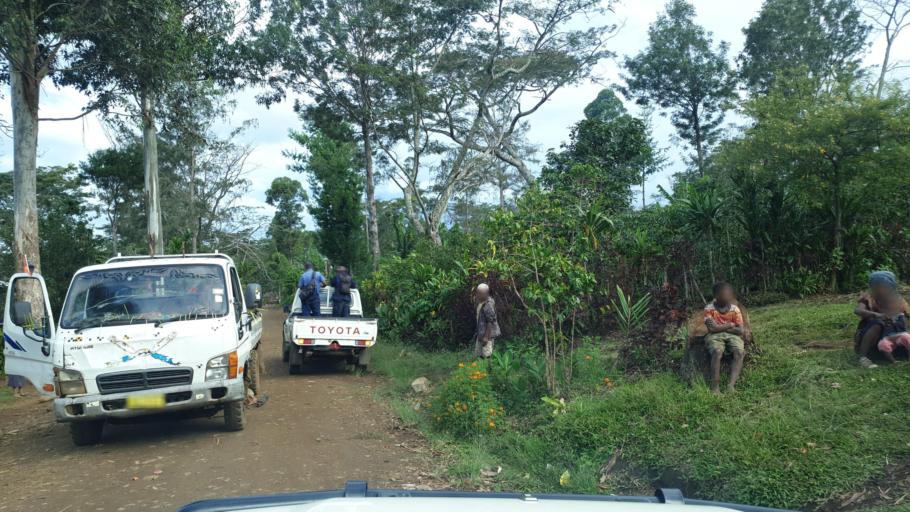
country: PG
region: Eastern Highlands
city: Goroka
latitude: -5.9377
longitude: 145.2677
